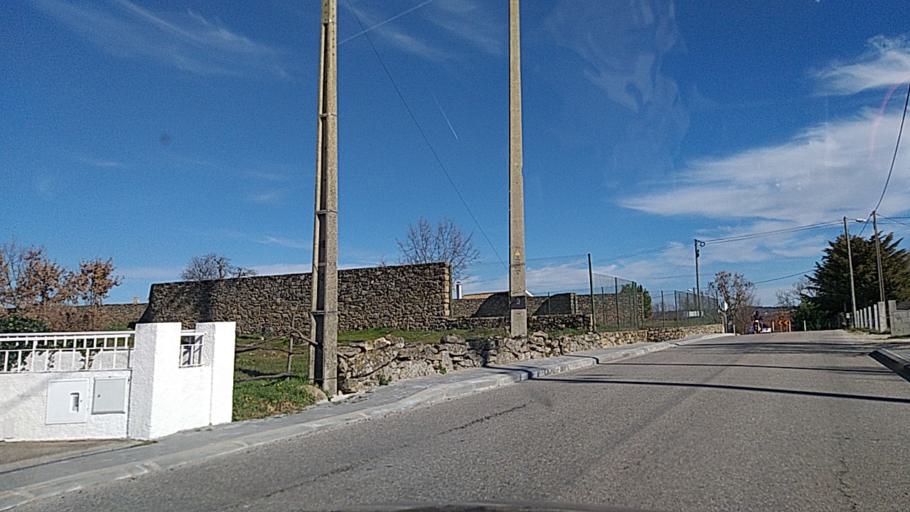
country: PT
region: Guarda
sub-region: Guarda
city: Sequeira
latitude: 40.6013
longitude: -7.0603
